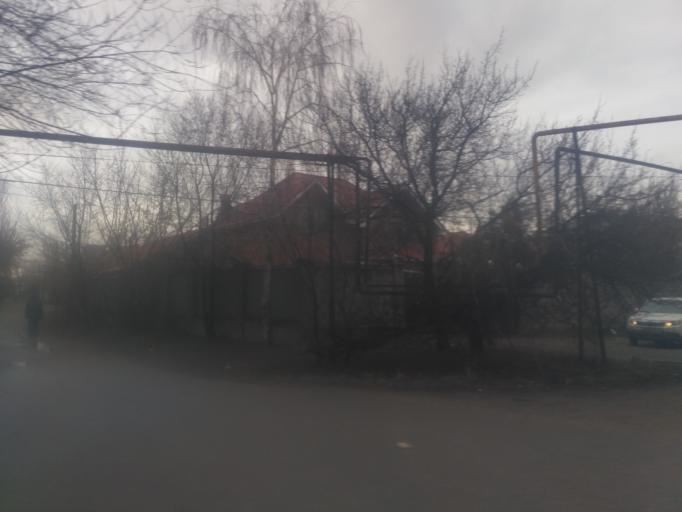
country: KZ
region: Almaty Oblysy
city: Burunday
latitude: 43.2190
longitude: 76.7438
